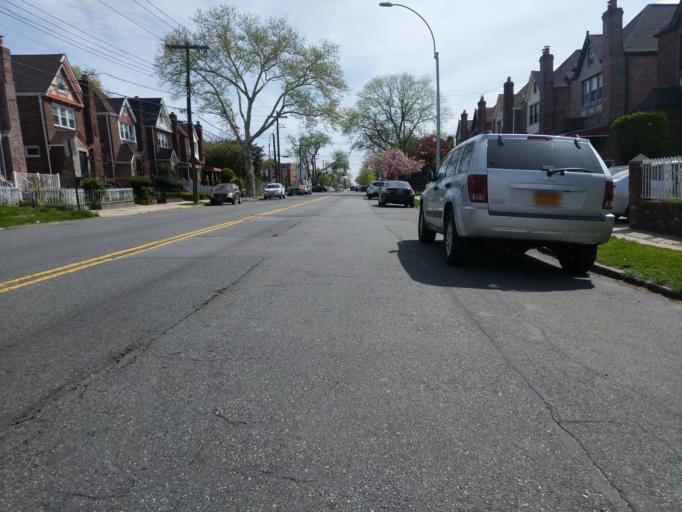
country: US
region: New York
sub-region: Nassau County
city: Bellerose Terrace
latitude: 40.7012
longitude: -73.7499
